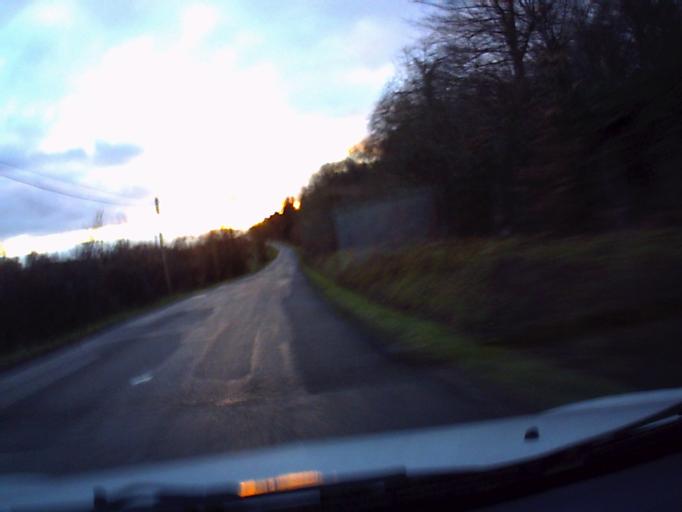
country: FR
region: Brittany
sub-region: Departement d'Ille-et-Vilaine
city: Iffendic
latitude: 48.1129
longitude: -2.0487
